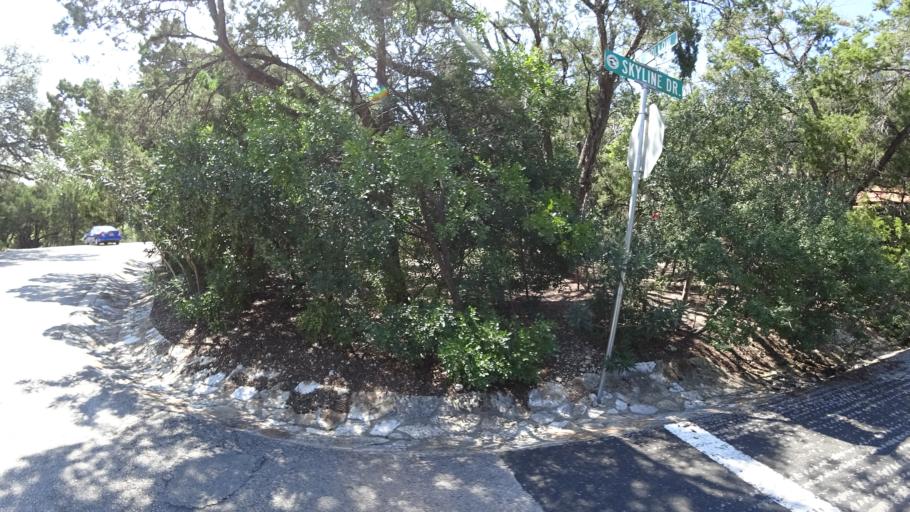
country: US
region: Texas
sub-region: Travis County
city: West Lake Hills
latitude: 30.2943
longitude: -97.7979
